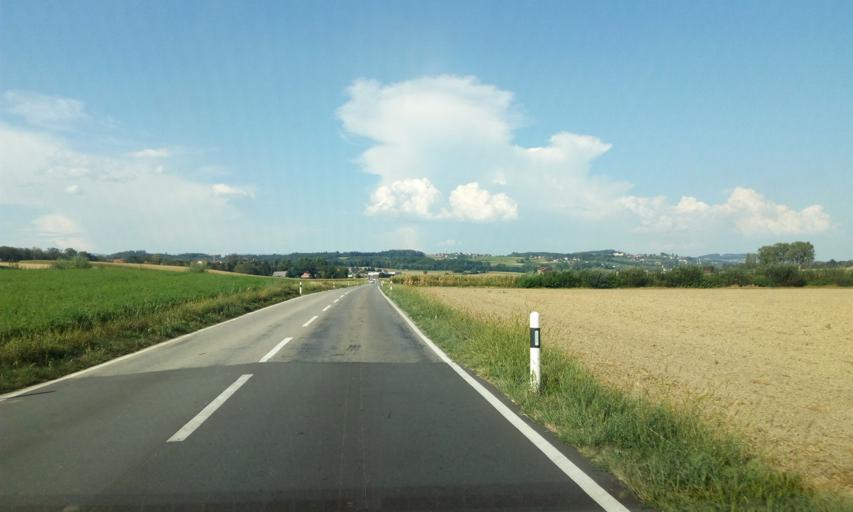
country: CH
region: Fribourg
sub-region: Broye District
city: Domdidier
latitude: 46.8925
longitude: 6.9883
